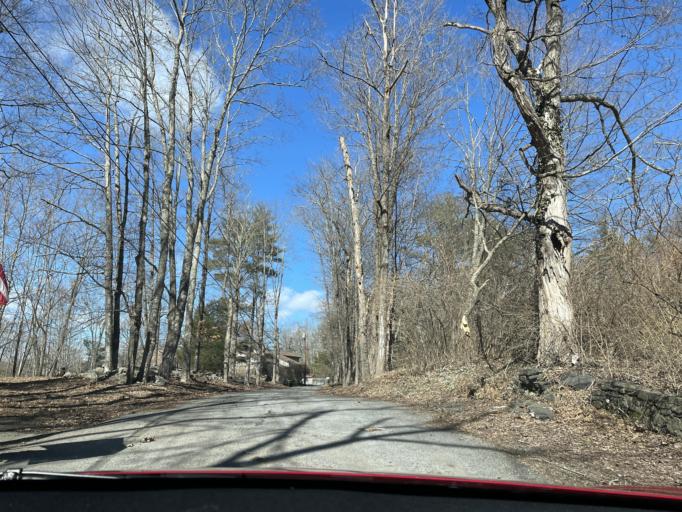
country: US
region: New York
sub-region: Ulster County
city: West Hurley
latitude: 41.9748
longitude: -74.0795
